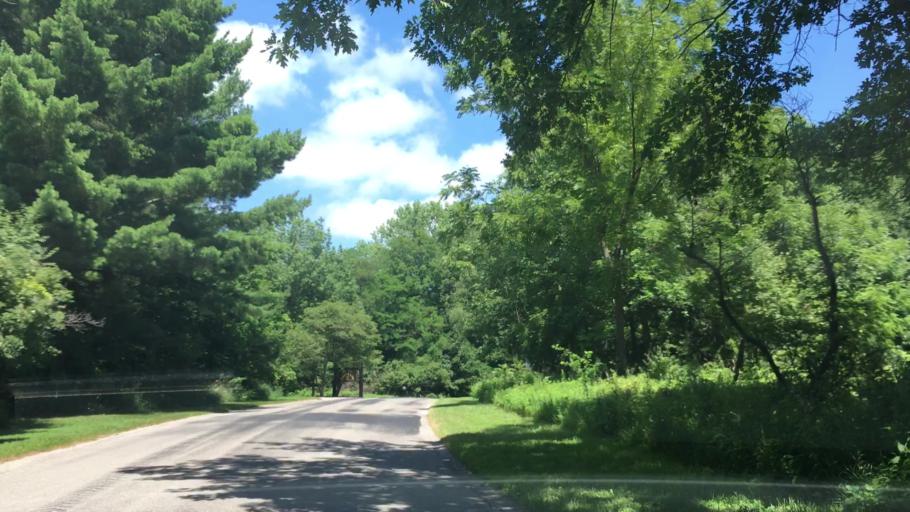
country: US
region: Iowa
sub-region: Johnson County
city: Tiffin
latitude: 41.7320
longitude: -91.7244
